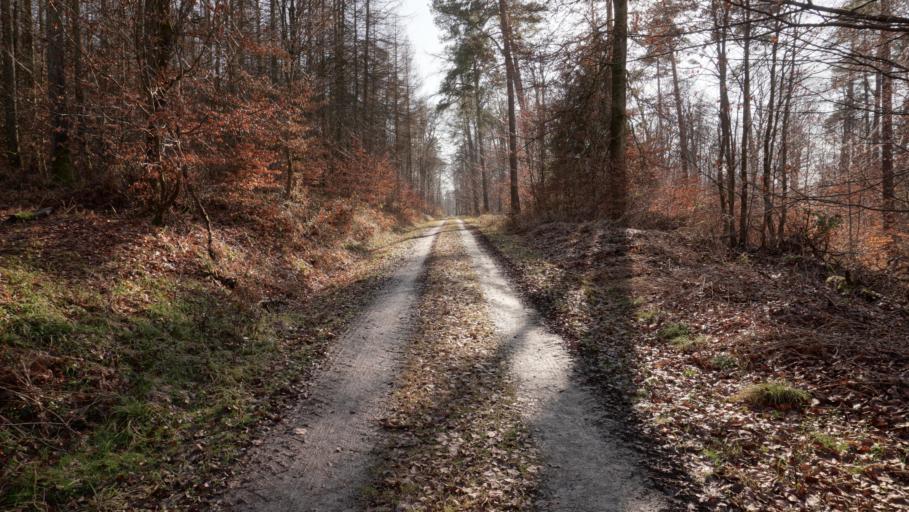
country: DE
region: Baden-Wuerttemberg
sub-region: Karlsruhe Region
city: Fahrenbach
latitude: 49.4307
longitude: 9.1303
